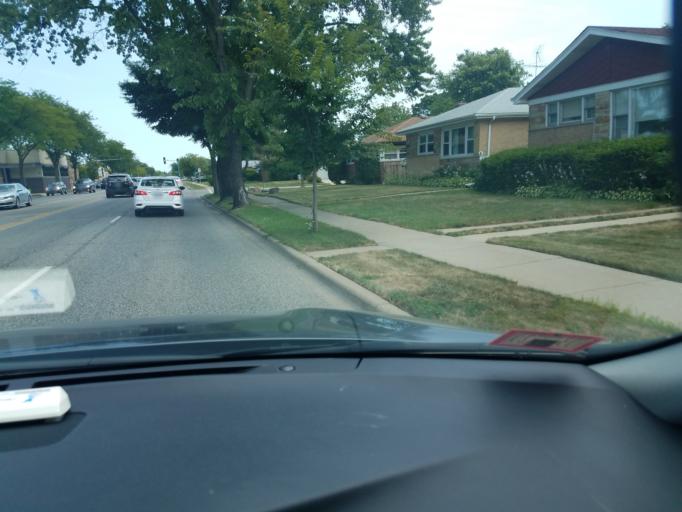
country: US
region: Illinois
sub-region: Cook County
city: Skokie
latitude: 42.0407
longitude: -87.7249
